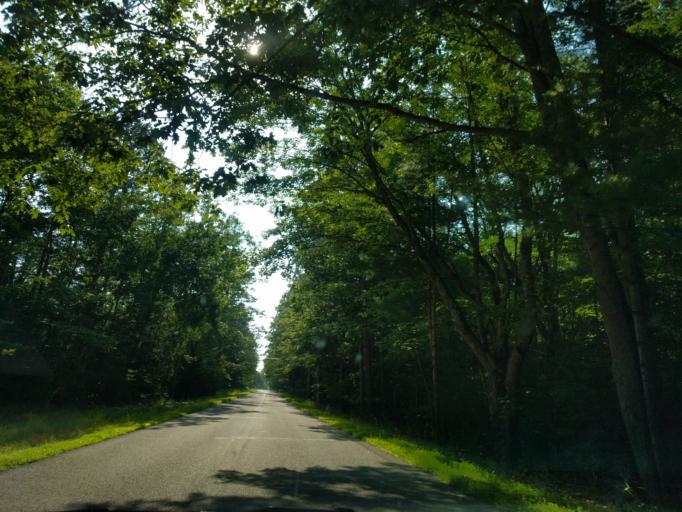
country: US
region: Michigan
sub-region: Delta County
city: Gladstone
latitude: 45.8913
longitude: -87.0510
